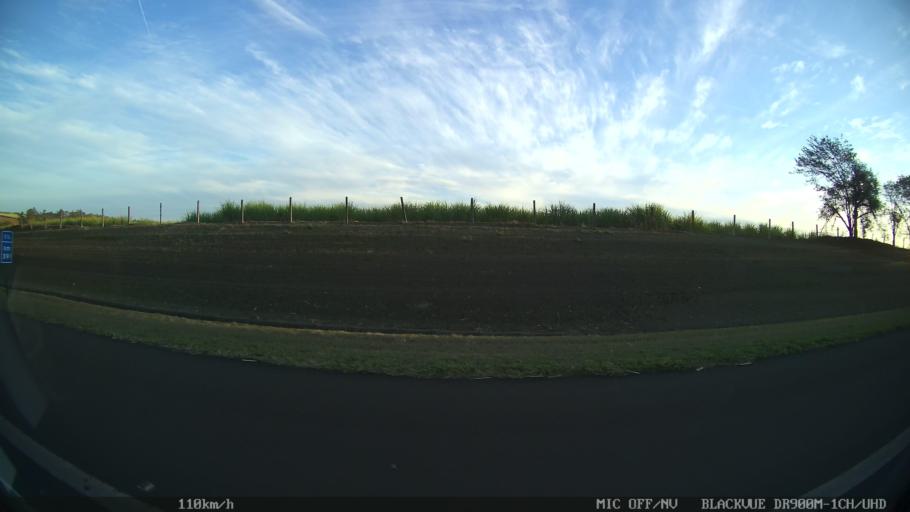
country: BR
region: Sao Paulo
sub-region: Catanduva
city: Catanduva
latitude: -21.1123
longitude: -49.0486
